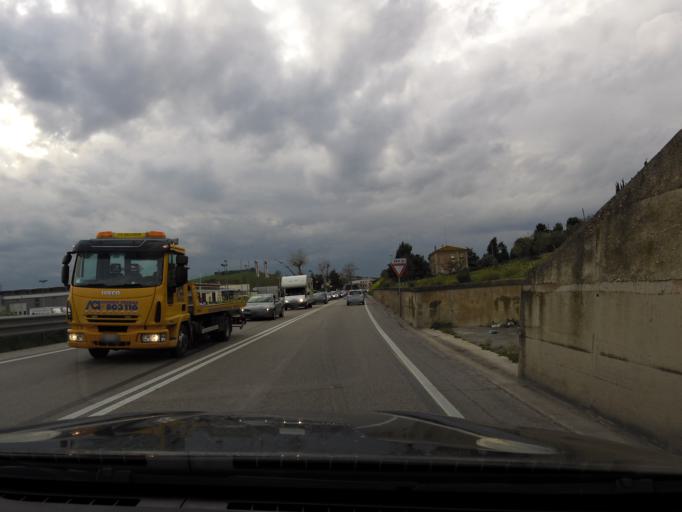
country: IT
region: The Marches
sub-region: Provincia di Macerata
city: Porto Recanati
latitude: 43.4349
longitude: 13.6489
